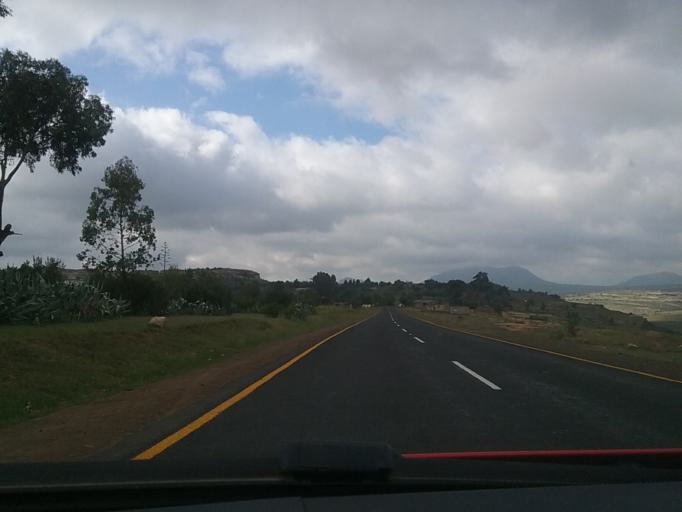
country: LS
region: Berea
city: Teyateyaneng
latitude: -29.1774
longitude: 27.7859
